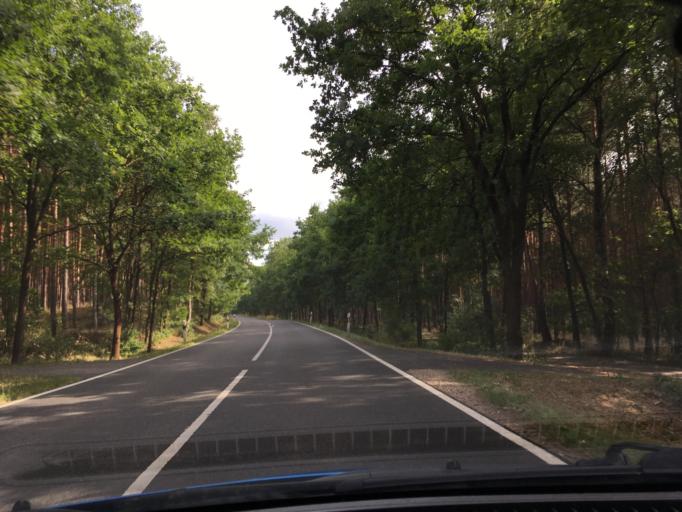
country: DE
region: Mecklenburg-Vorpommern
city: Lubtheen
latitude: 53.2895
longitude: 11.0925
